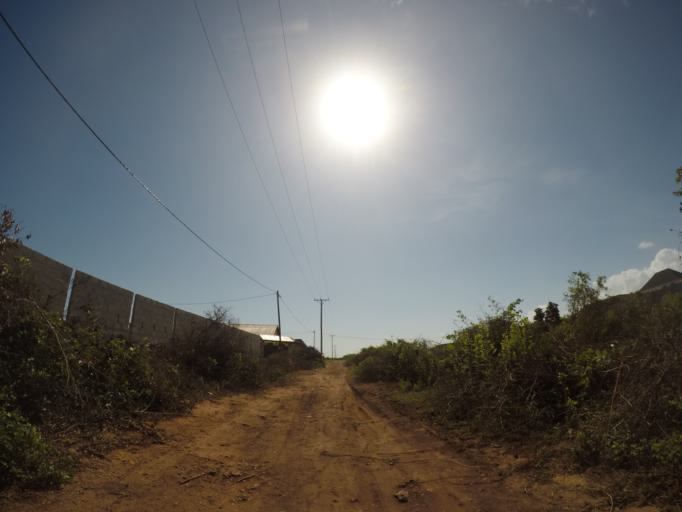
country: TZ
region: Zanzibar Central/South
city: Koani
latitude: -6.2091
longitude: 39.3024
